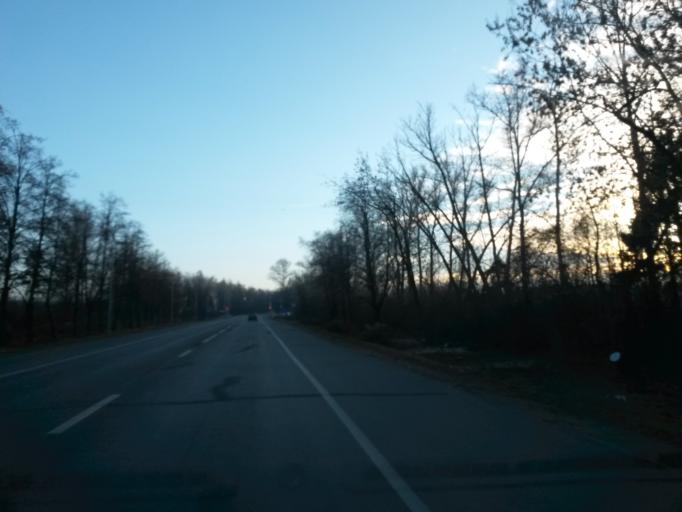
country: RU
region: Moskovskaya
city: Stolbovaya
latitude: 55.2595
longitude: 37.5091
